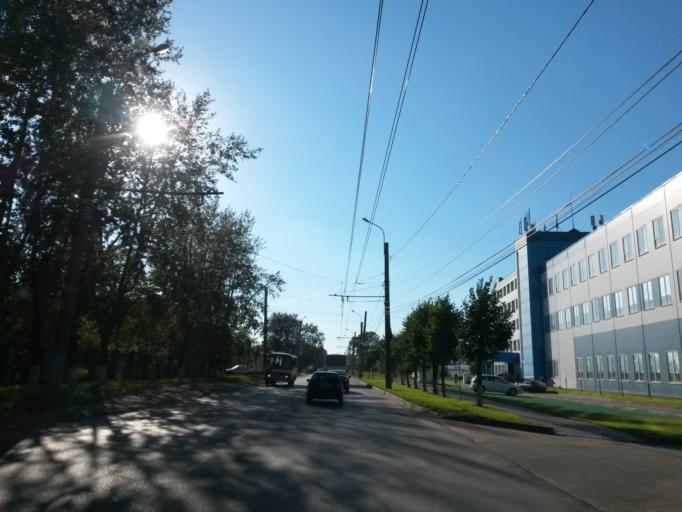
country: RU
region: Ivanovo
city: Novo-Talitsy
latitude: 56.9988
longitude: 40.9114
